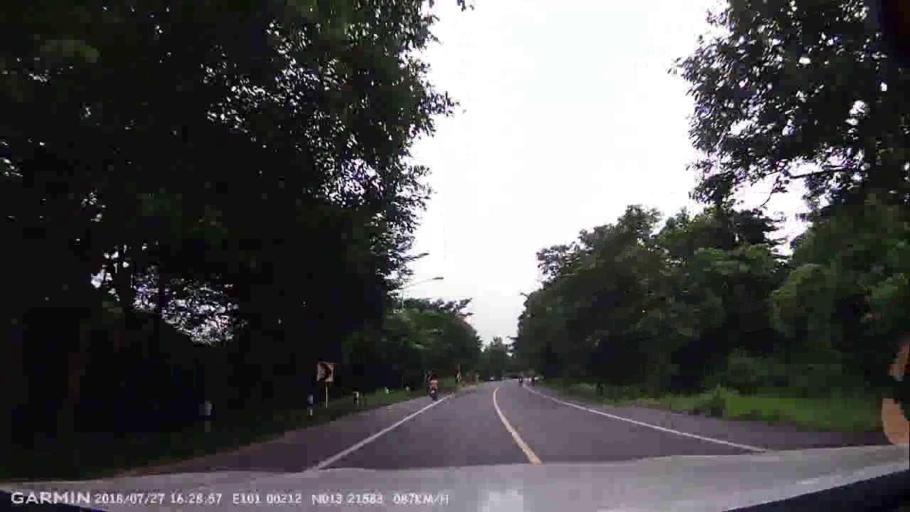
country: TH
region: Chon Buri
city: Si Racha
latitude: 13.2156
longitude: 101.0022
